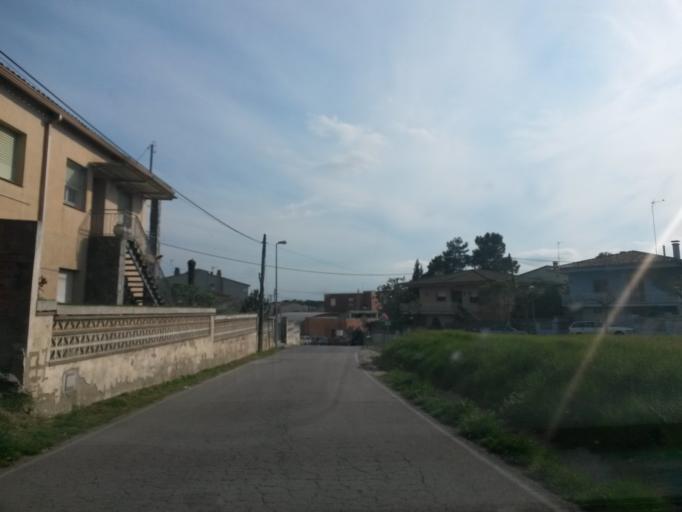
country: ES
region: Catalonia
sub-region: Provincia de Girona
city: Caldes de Malavella
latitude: 41.8422
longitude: 2.8102
